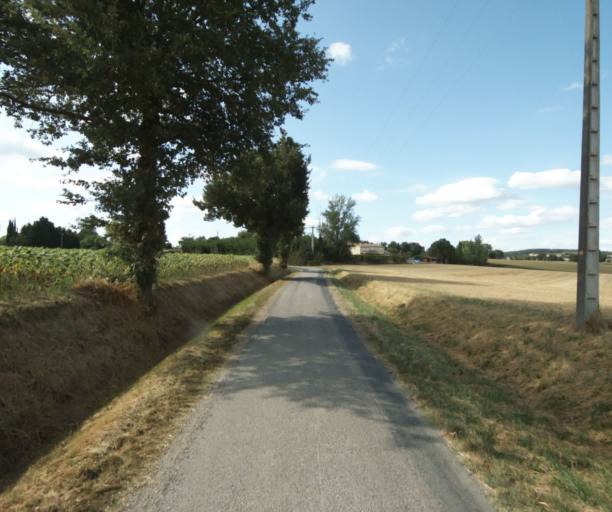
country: FR
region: Midi-Pyrenees
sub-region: Departement du Tarn
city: Puylaurens
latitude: 43.5321
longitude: 1.9916
